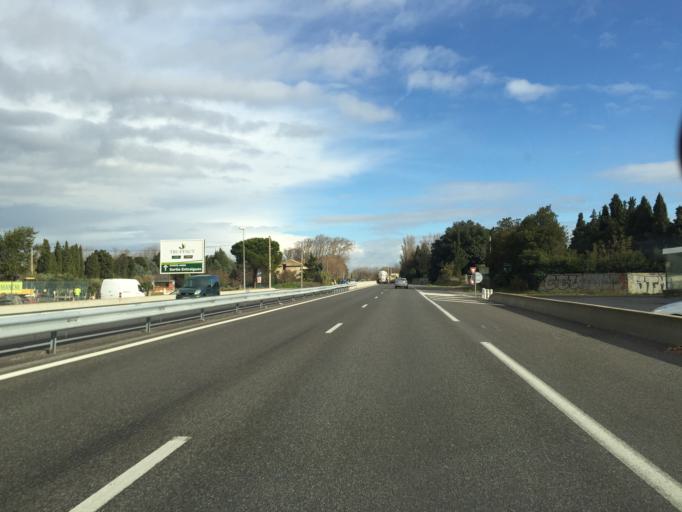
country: FR
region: Provence-Alpes-Cote d'Azur
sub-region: Departement du Vaucluse
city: Vedene
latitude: 43.9889
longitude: 4.9013
